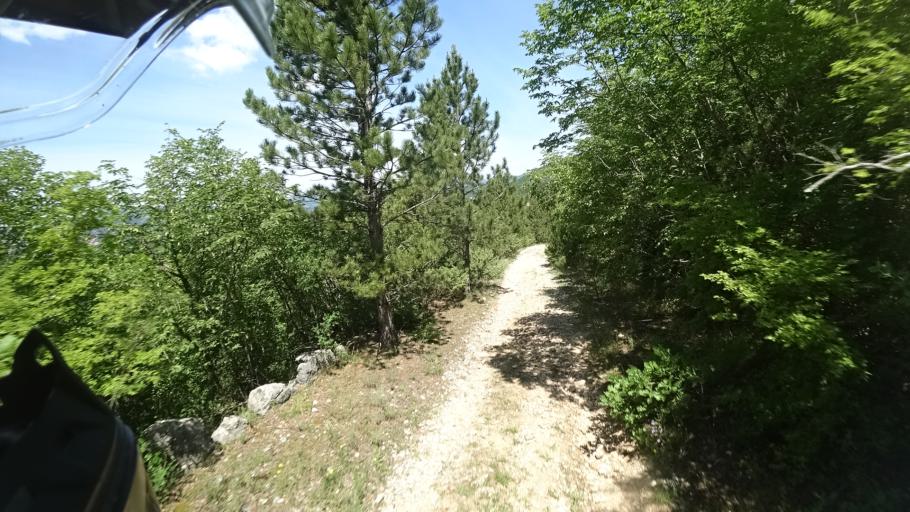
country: HR
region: Sibensko-Kniniska
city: Knin
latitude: 44.0349
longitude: 16.2296
